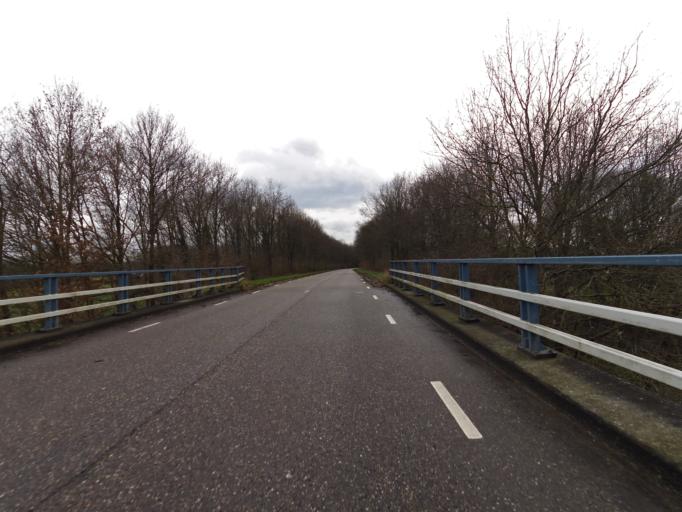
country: NL
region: Gelderland
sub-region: Oude IJsselstreek
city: Wisch
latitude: 51.9446
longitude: 6.3714
